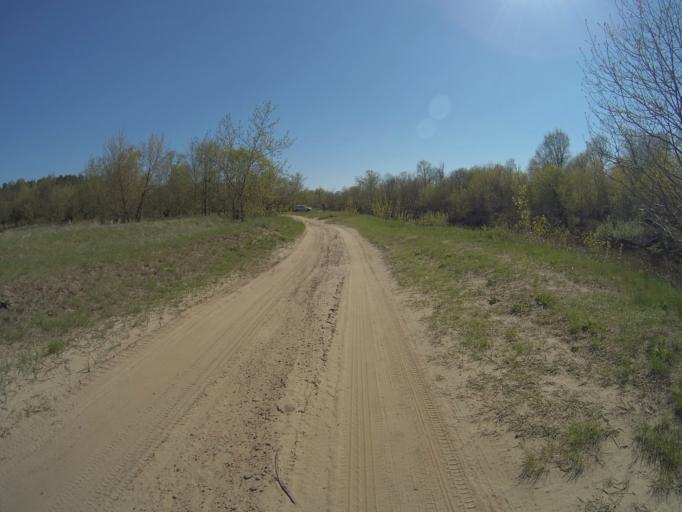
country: RU
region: Vladimir
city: Sudogda
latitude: 56.1476
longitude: 40.8138
